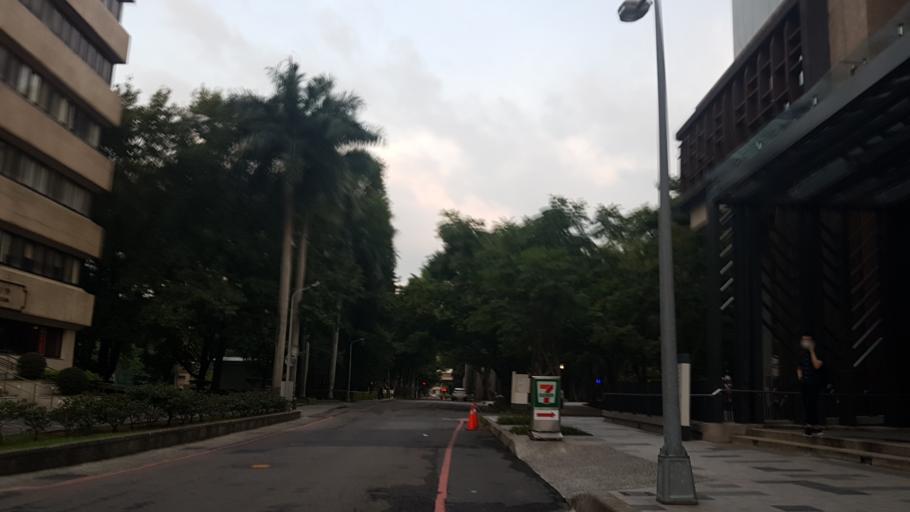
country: TW
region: Taipei
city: Taipei
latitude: 25.0146
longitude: 121.5382
